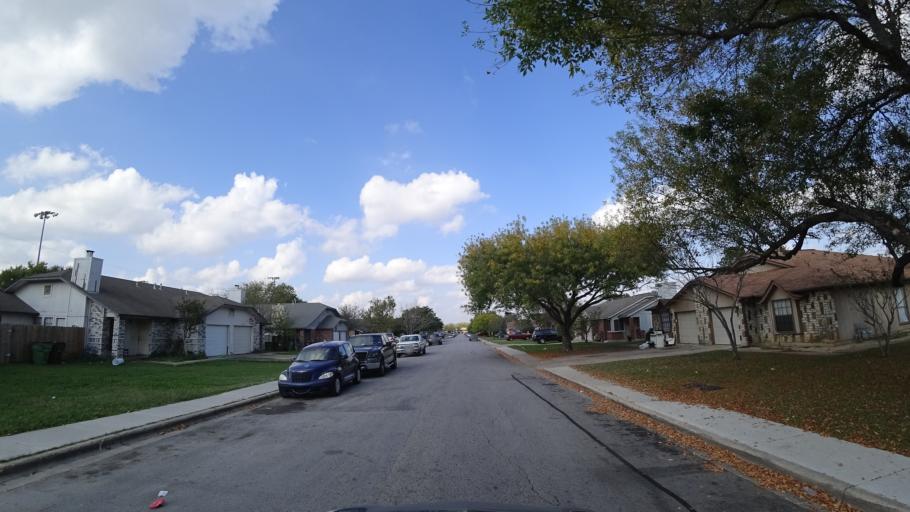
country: US
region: Texas
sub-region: Williamson County
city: Round Rock
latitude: 30.4984
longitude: -97.6707
